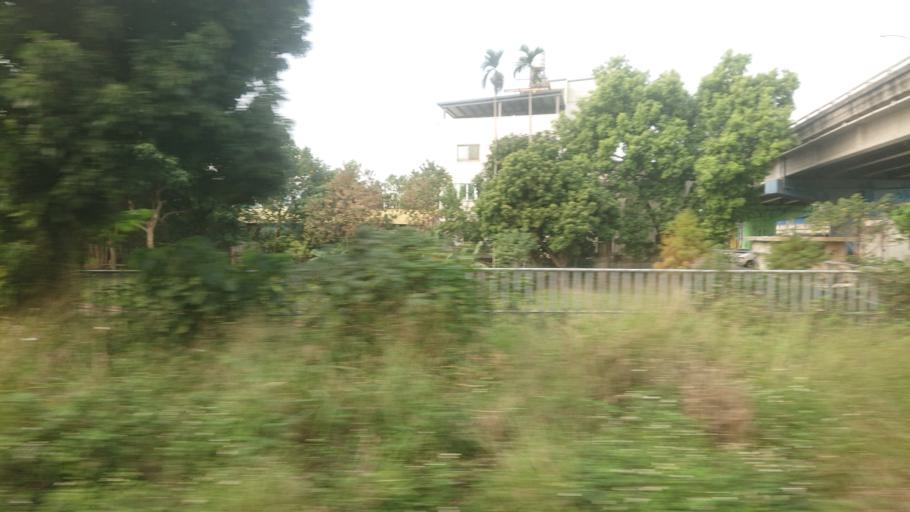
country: TW
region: Taiwan
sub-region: Nantou
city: Nantou
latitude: 23.8534
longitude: 120.5934
